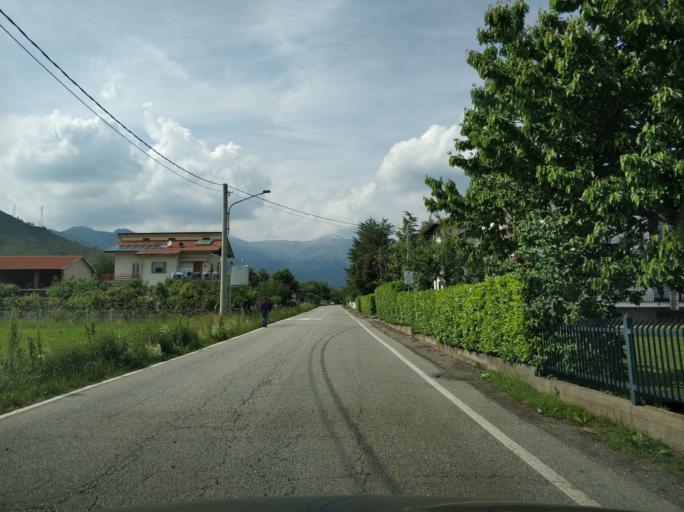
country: IT
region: Piedmont
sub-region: Provincia di Torino
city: Corio
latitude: 45.2884
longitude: 7.5524
